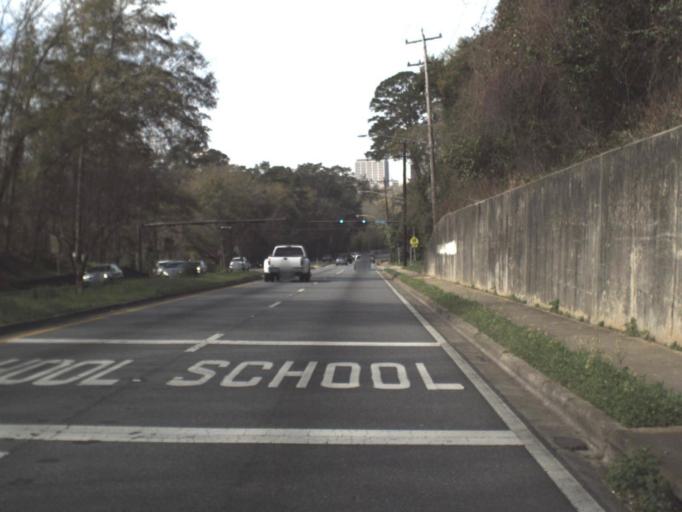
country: US
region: Florida
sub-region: Leon County
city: Tallahassee
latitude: 30.4459
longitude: -84.2675
